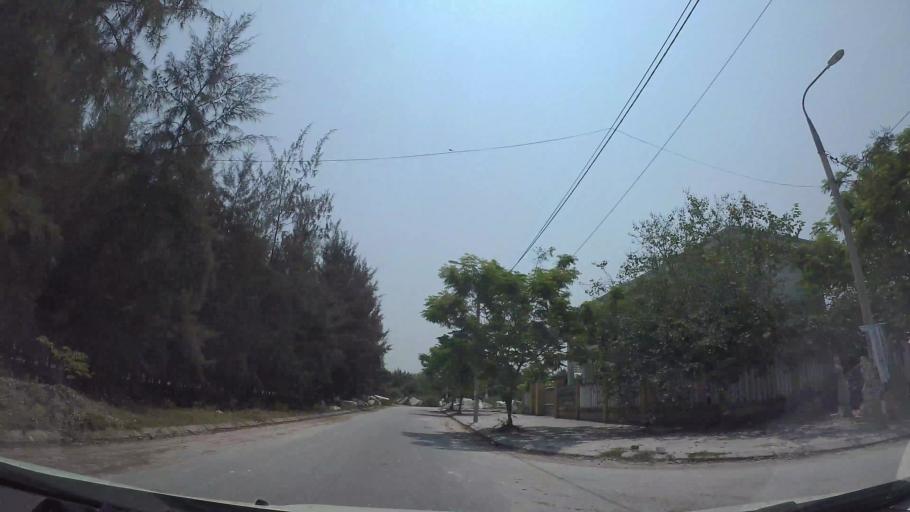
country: VN
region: Da Nang
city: Ngu Hanh Son
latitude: 15.9920
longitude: 108.2538
